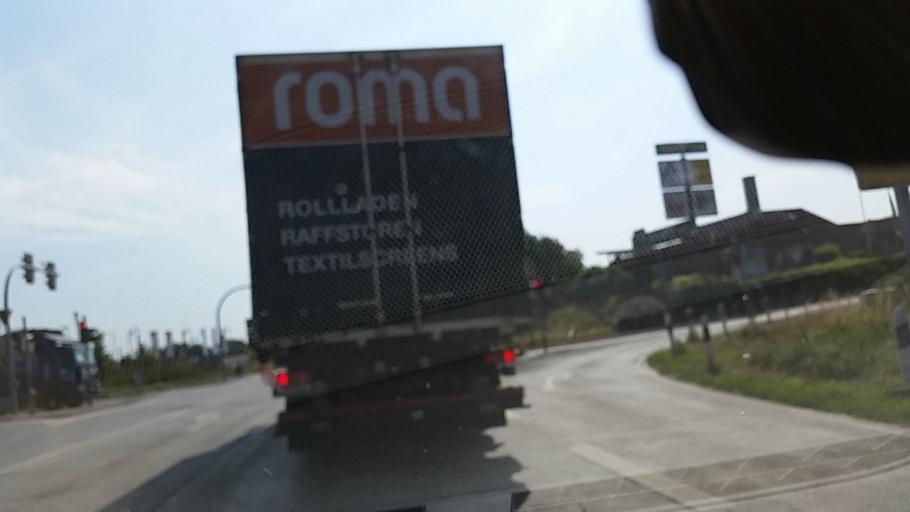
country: DE
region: Lower Saxony
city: Steinfeld
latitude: 52.5920
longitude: 8.2164
